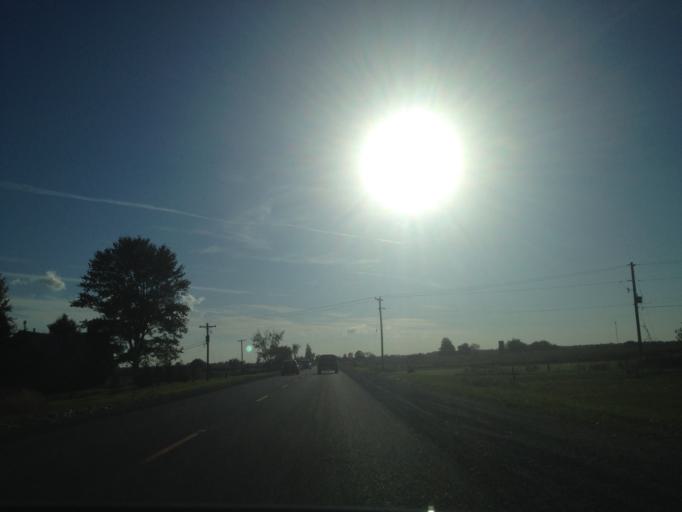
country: CA
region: Ontario
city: Delaware
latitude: 42.6370
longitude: -81.5611
